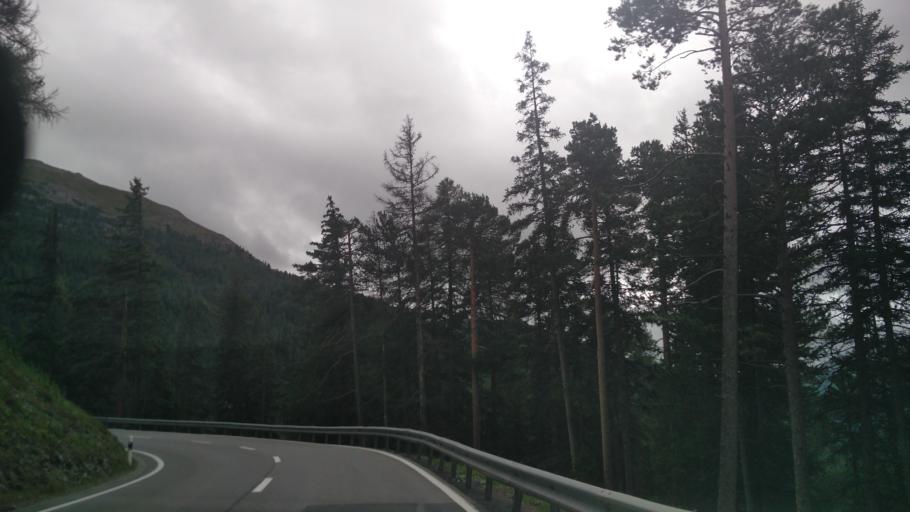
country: CH
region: Grisons
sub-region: Inn District
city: Zernez
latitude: 46.6911
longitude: 10.1374
